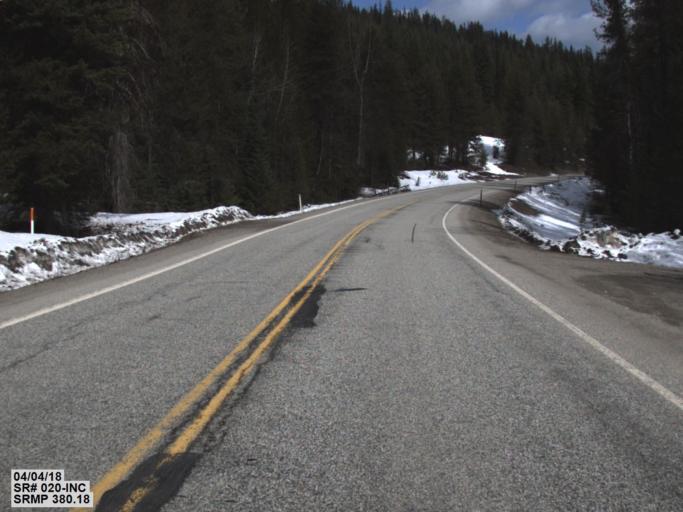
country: US
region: Washington
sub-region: Stevens County
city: Colville
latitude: 48.6263
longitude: -117.5453
